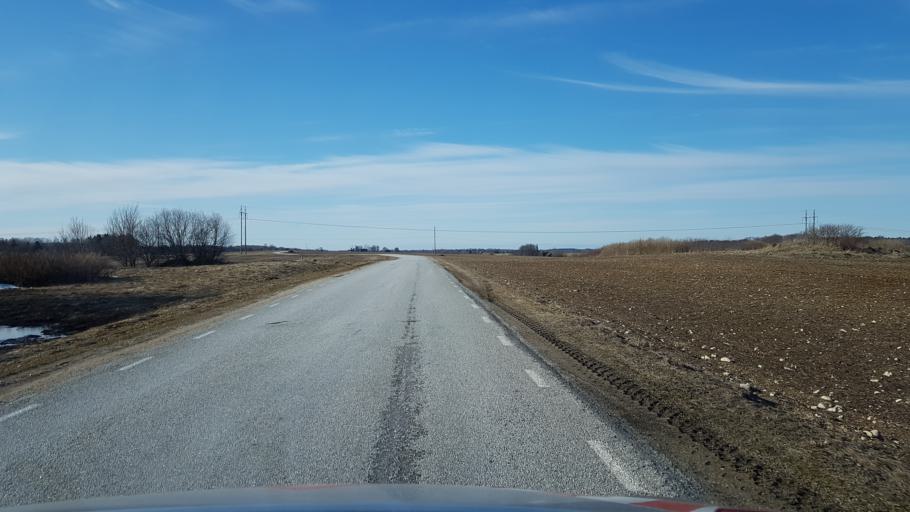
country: EE
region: Laeaene-Virumaa
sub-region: Kadrina vald
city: Kadrina
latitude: 59.2801
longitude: 26.1881
